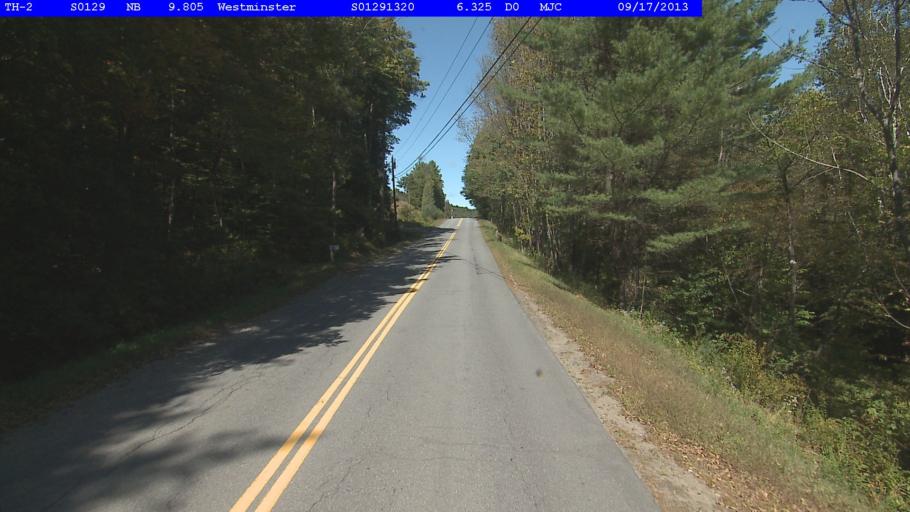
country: US
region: Vermont
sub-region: Windham County
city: Rockingham
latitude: 43.1055
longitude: -72.5380
